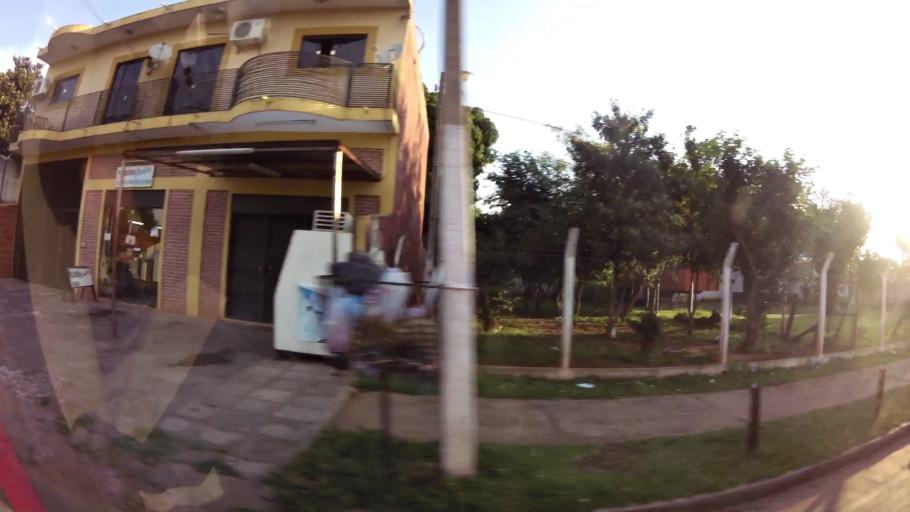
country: PY
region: Central
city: San Lorenzo
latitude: -25.3591
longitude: -57.5116
